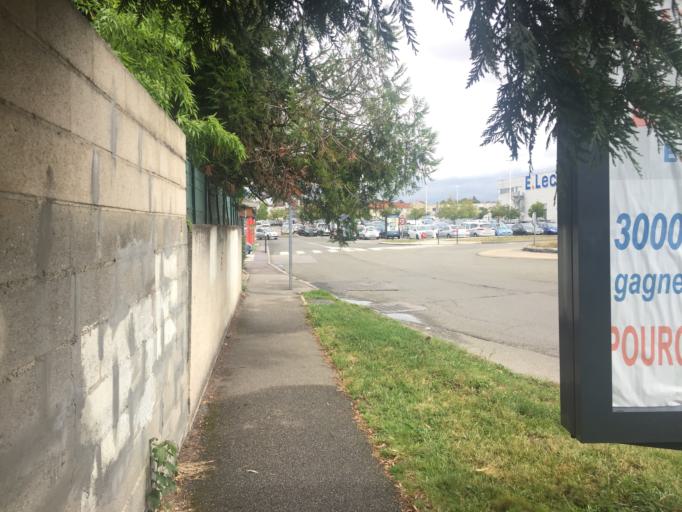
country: FR
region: Ile-de-France
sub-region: Departement des Yvelines
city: Bois-d'Arcy
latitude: 48.7982
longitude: 2.0350
